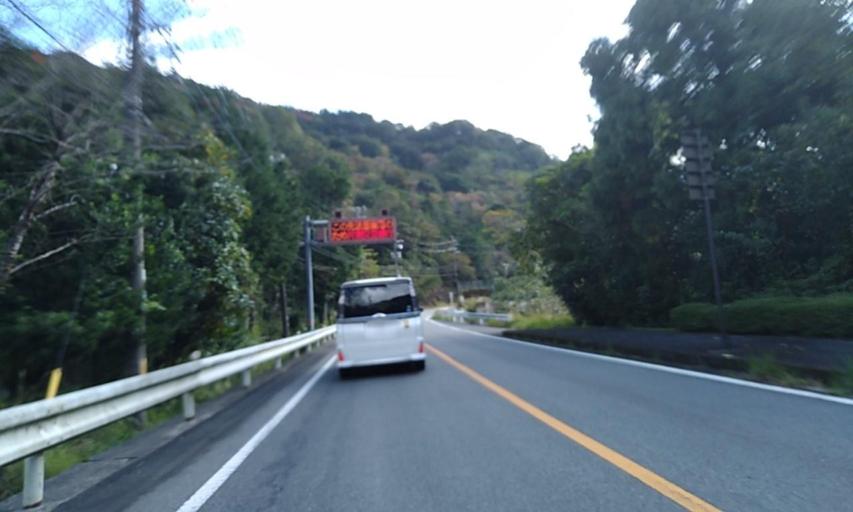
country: JP
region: Mie
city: Owase
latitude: 34.2133
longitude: 136.3549
